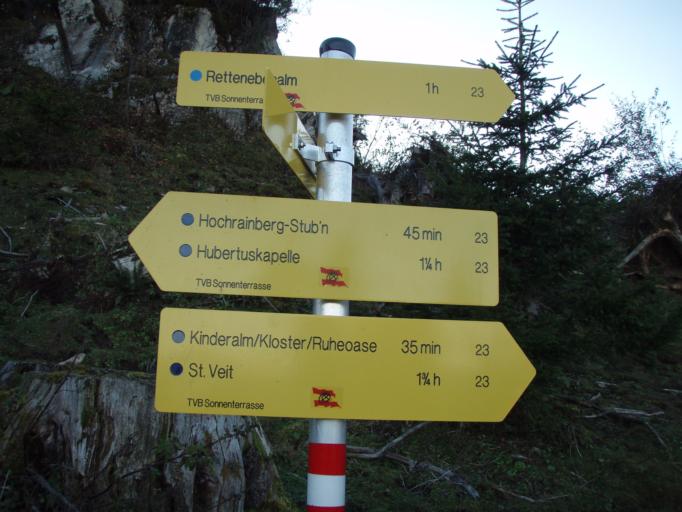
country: AT
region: Salzburg
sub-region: Politischer Bezirk Sankt Johann im Pongau
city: Sankt Veit im Pongau
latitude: 47.3459
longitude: 13.1476
